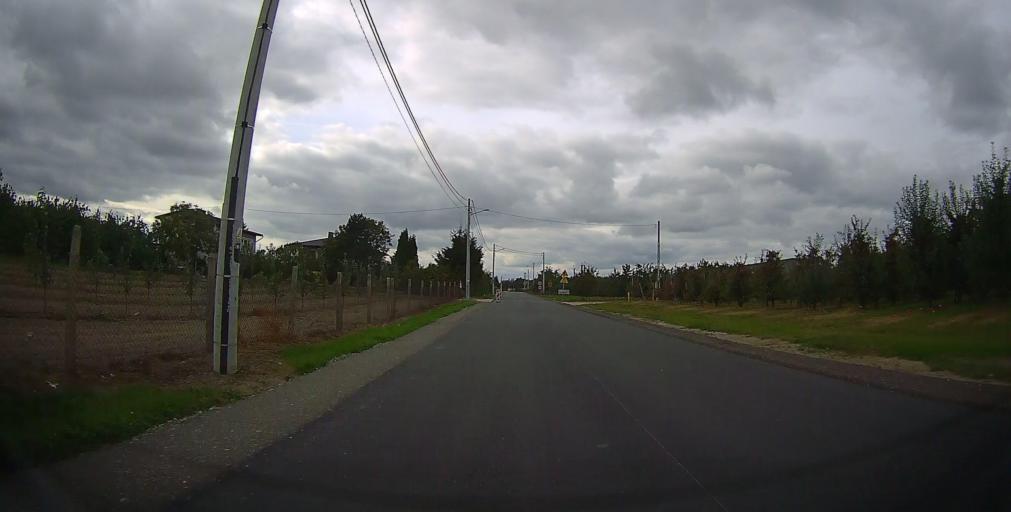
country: PL
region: Masovian Voivodeship
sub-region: Powiat grojecki
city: Belsk Duzy
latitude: 51.8099
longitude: 20.8415
